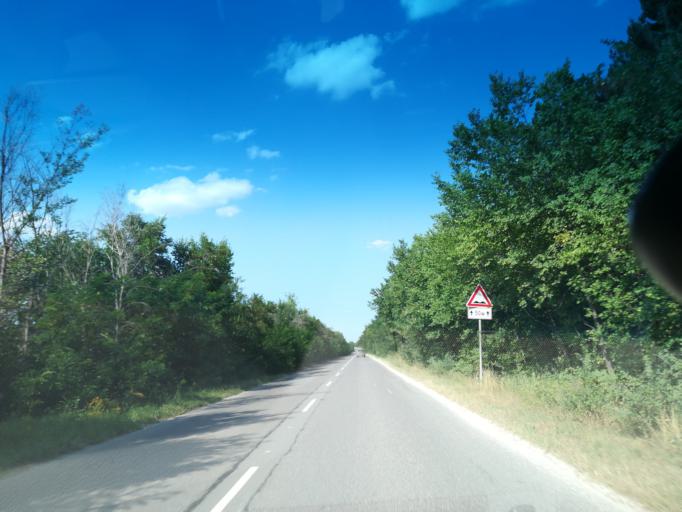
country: BG
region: Stara Zagora
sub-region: Obshtina Chirpan
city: Chirpan
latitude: 42.2427
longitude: 25.4059
